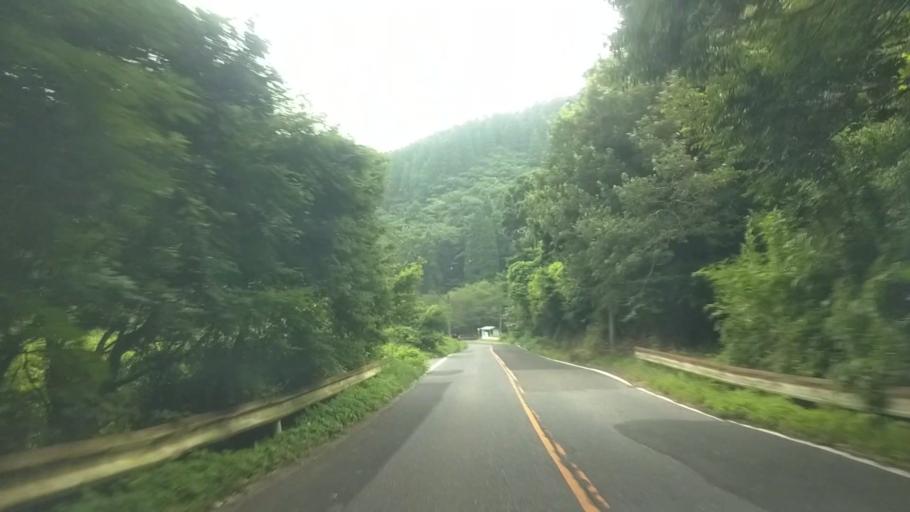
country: JP
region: Chiba
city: Tateyama
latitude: 35.1406
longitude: 139.9018
